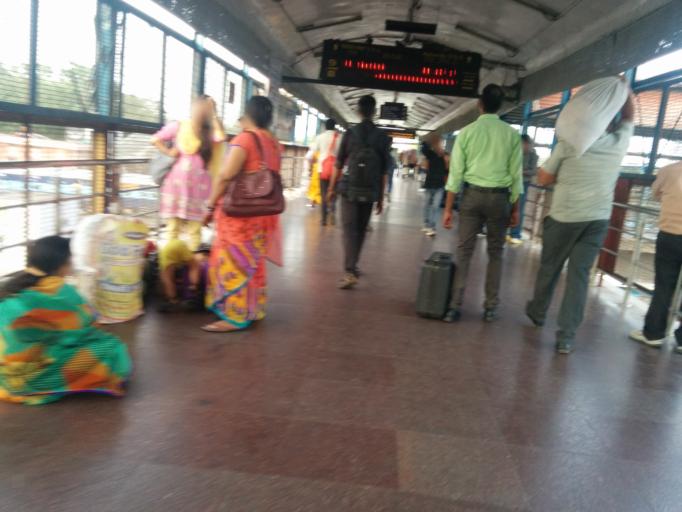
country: IN
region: NCT
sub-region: New Delhi
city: New Delhi
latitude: 28.6437
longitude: 77.2200
